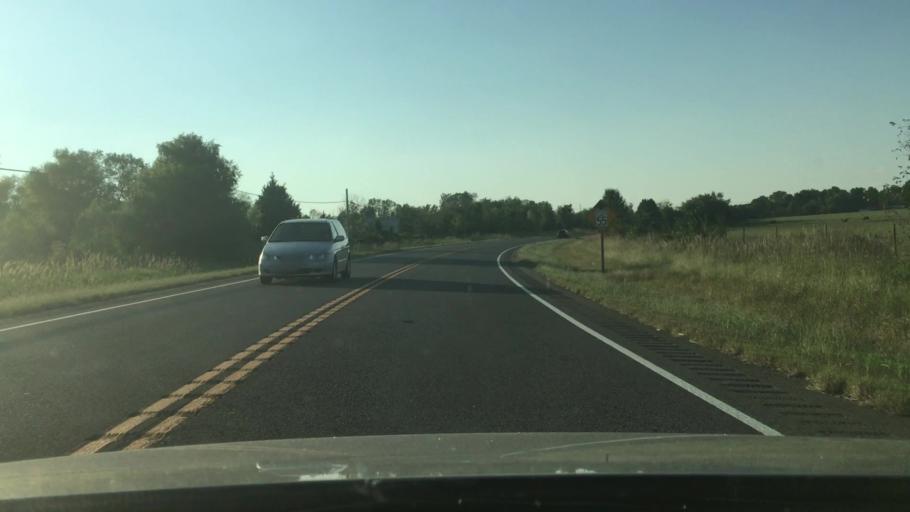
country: US
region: Oklahoma
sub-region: Wagoner County
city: Wagoner
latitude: 35.9387
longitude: -95.3601
